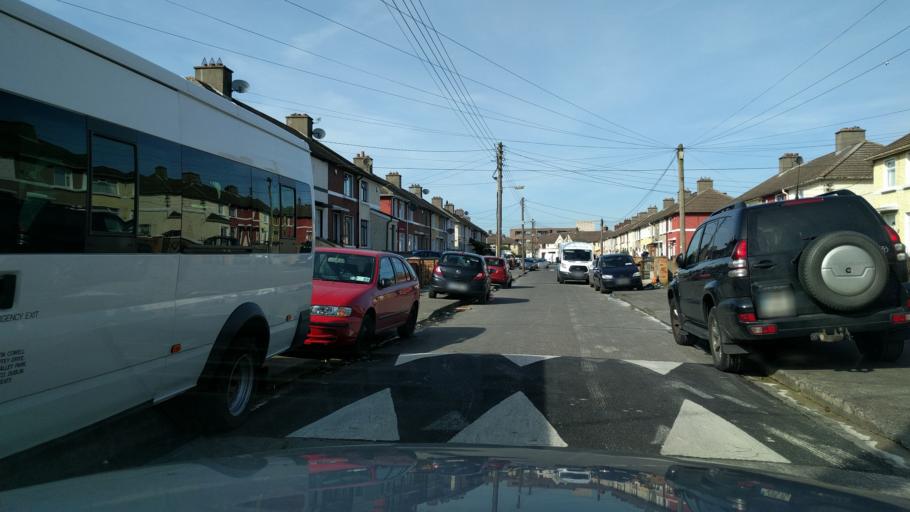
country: IE
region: Leinster
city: Chapelizod
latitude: 53.3400
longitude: -6.3497
